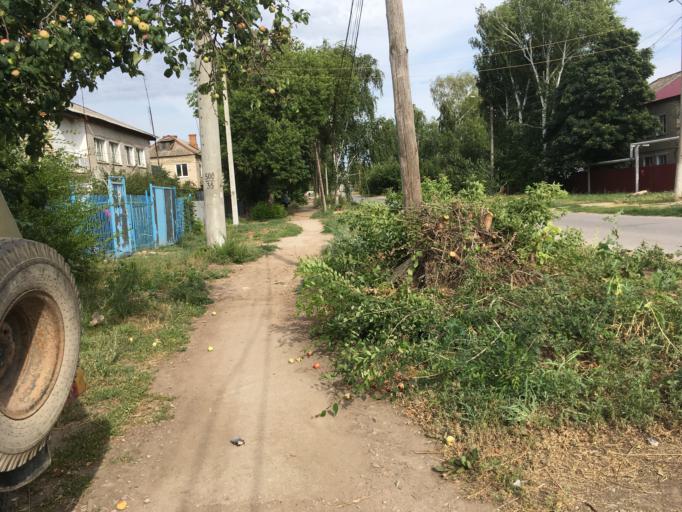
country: RU
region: Samara
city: Bezenchuk
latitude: 52.9883
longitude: 49.4423
